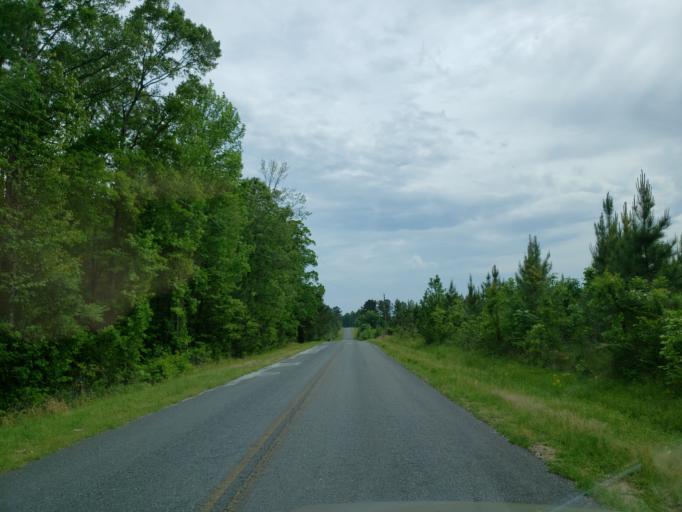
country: US
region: Georgia
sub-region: Bibb County
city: West Point
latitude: 32.8610
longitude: -83.8918
